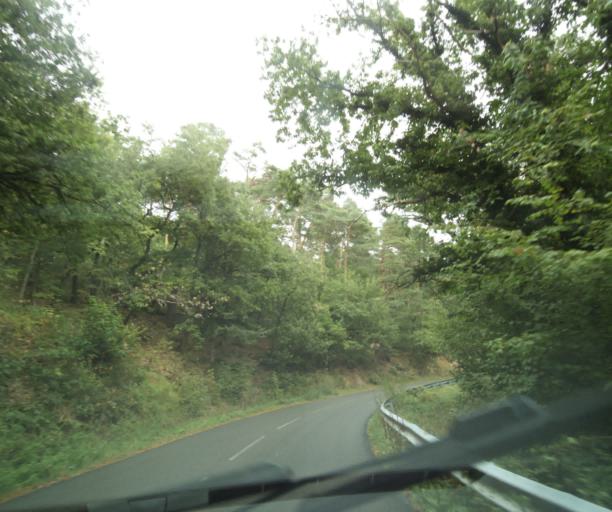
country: FR
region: Auvergne
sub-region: Departement du Puy-de-Dome
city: Durtol
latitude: 45.7943
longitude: 3.0407
